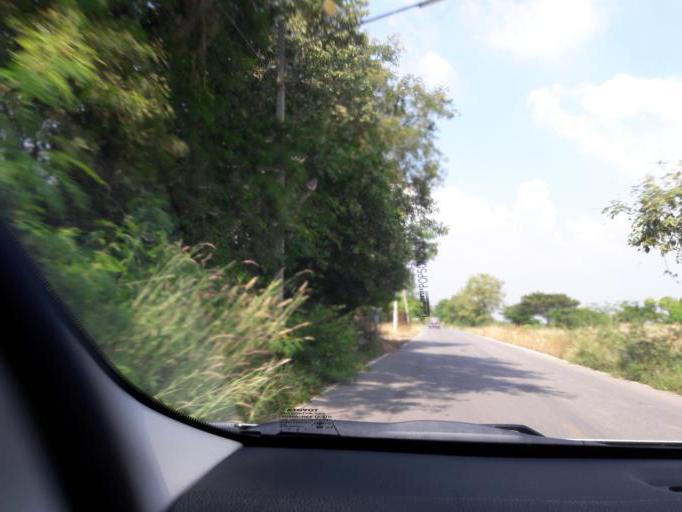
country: TH
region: Ang Thong
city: Ang Thong
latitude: 14.5892
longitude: 100.3999
